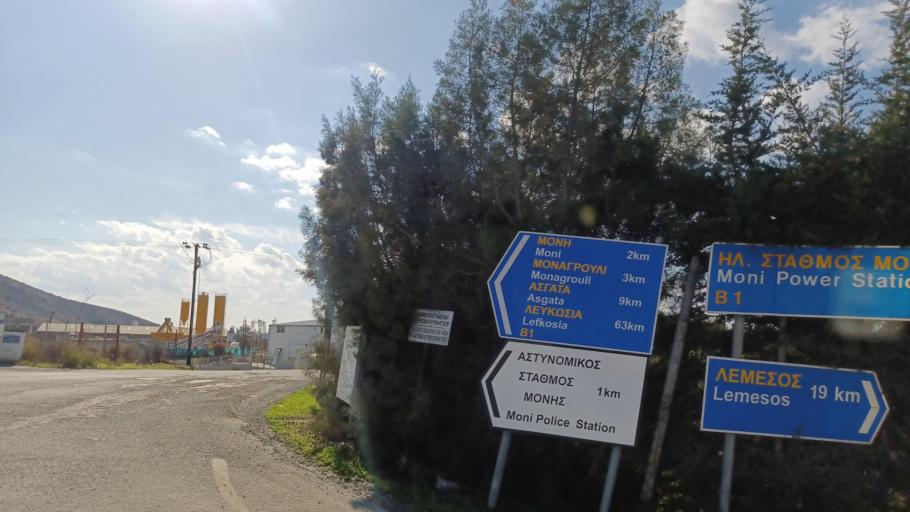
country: CY
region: Limassol
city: Pyrgos
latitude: 34.7206
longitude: 33.2013
